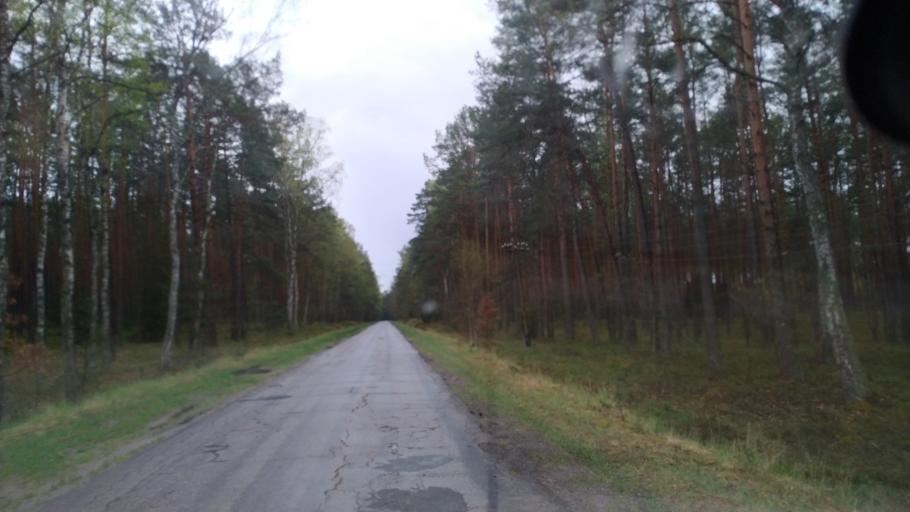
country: PL
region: Pomeranian Voivodeship
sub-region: Powiat starogardzki
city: Osiek
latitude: 53.6682
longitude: 18.4795
